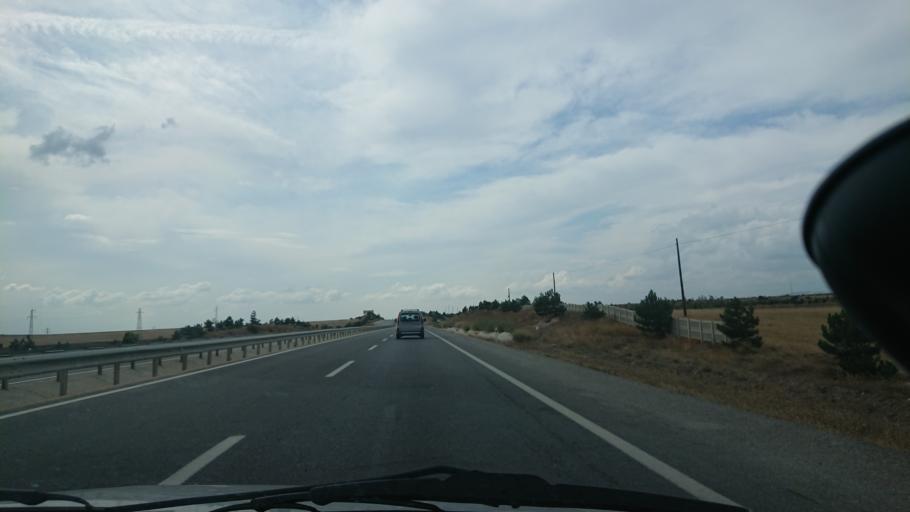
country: TR
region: Eskisehir
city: Inonu
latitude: 39.7224
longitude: 30.2499
